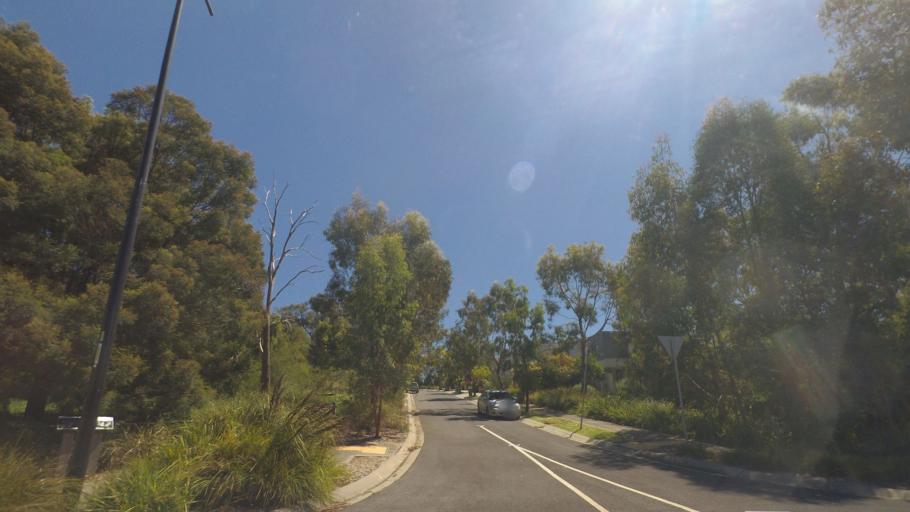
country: AU
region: Victoria
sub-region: Maroondah
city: Croydon North
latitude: -37.7804
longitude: 145.2996
